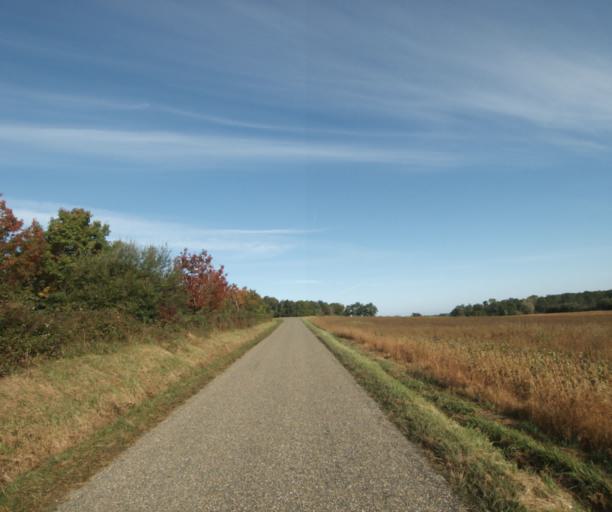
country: FR
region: Midi-Pyrenees
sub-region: Departement du Gers
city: Eauze
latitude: 43.9305
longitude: 0.1234
